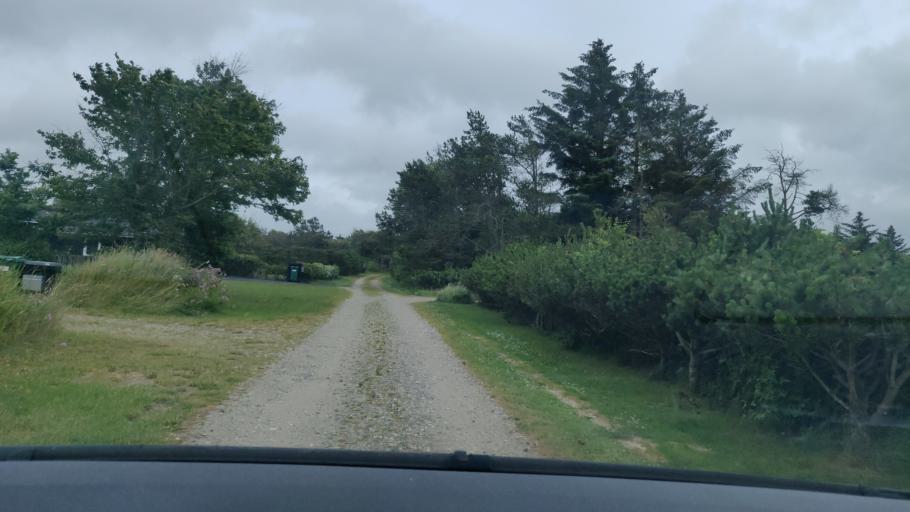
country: DK
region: North Denmark
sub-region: Jammerbugt Kommune
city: Pandrup
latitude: 57.2571
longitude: 9.6029
